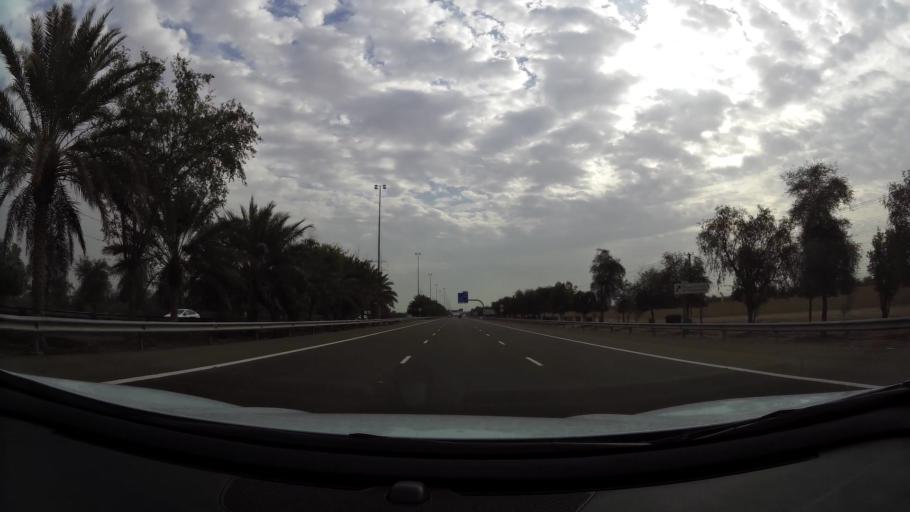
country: AE
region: Abu Dhabi
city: Al Ain
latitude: 24.2096
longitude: 55.4516
